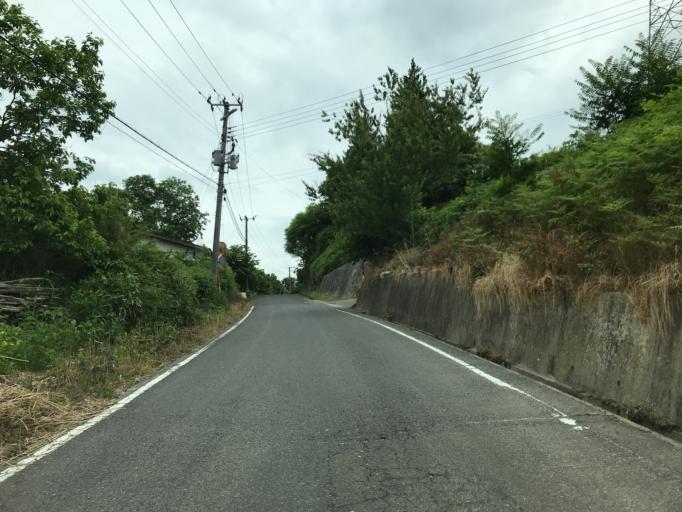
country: JP
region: Fukushima
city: Miharu
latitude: 37.3984
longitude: 140.5361
